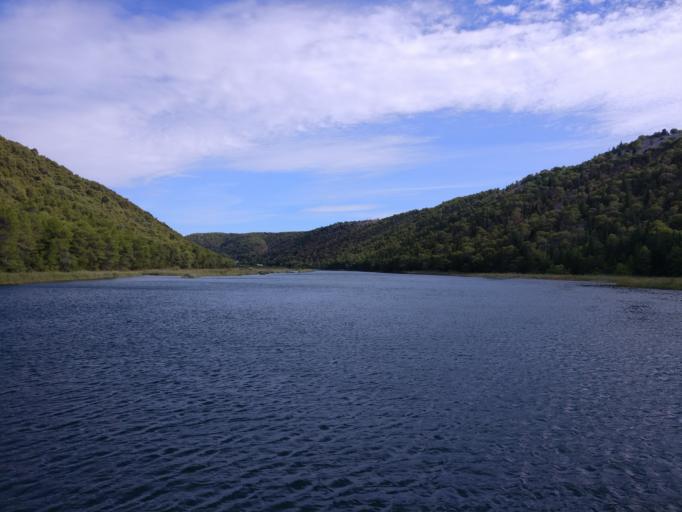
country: HR
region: Sibensko-Kniniska
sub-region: Grad Sibenik
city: Sibenik
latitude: 43.8188
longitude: 15.9487
